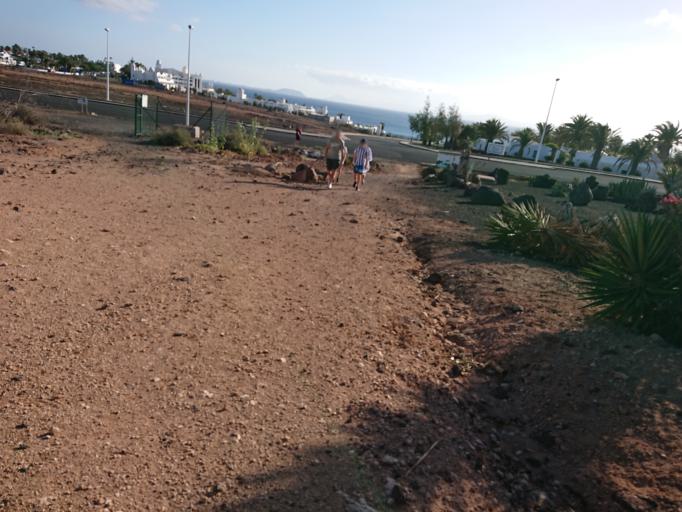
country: ES
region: Canary Islands
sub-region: Provincia de Las Palmas
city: Playa Blanca
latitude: 28.8642
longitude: -13.8461
